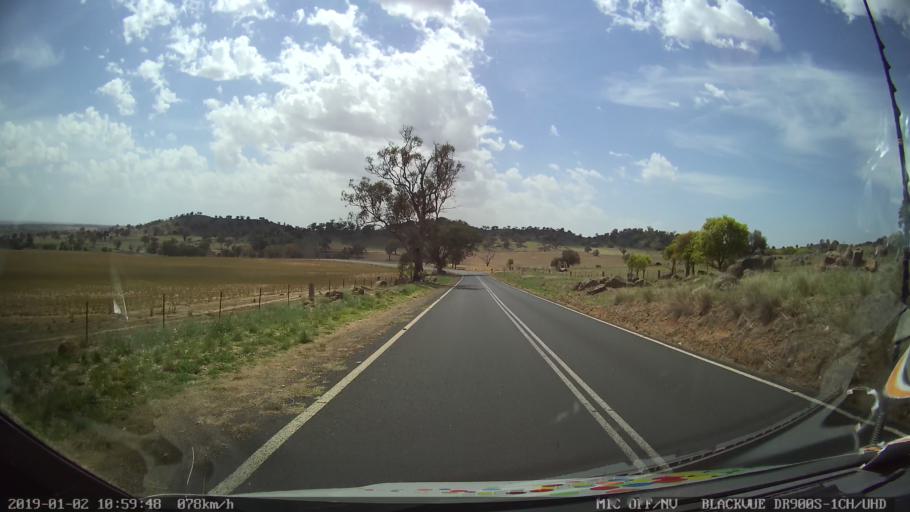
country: AU
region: New South Wales
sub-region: Cootamundra
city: Cootamundra
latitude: -34.6120
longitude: 148.3100
